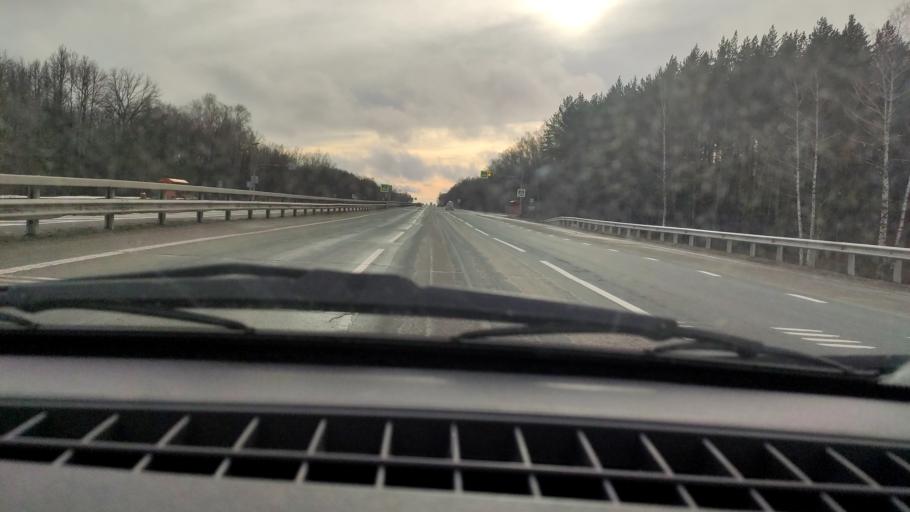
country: RU
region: Bashkortostan
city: Avdon
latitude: 54.6482
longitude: 55.6437
